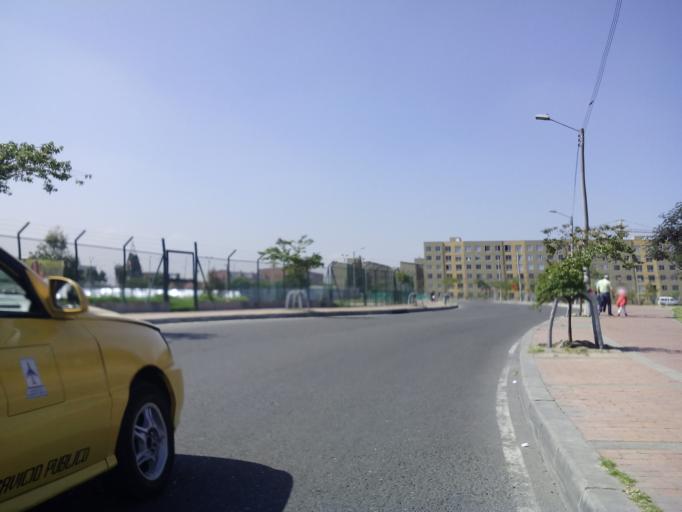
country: CO
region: Bogota D.C.
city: Bogota
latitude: 4.6466
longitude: -74.1537
